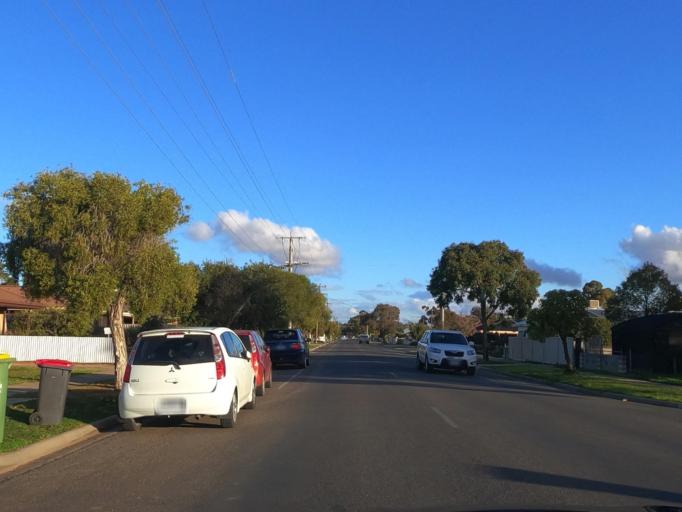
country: AU
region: Victoria
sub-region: Swan Hill
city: Swan Hill
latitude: -35.3415
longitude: 143.5440
